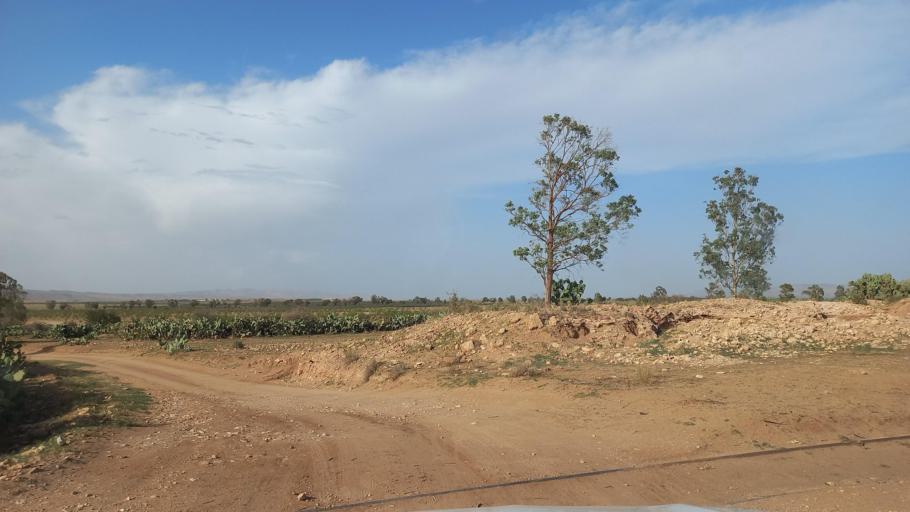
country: TN
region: Al Qasrayn
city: Kasserine
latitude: 35.2248
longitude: 8.9694
